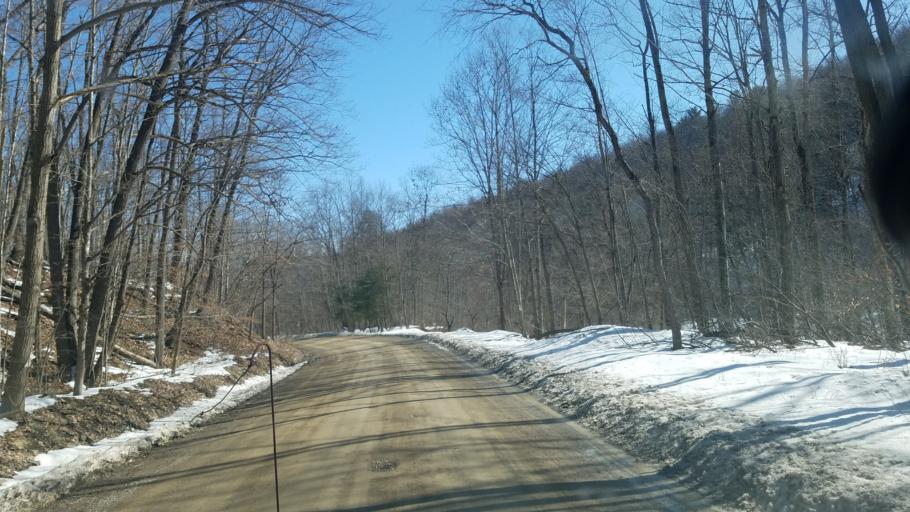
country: US
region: New York
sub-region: Allegany County
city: Alfred
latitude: 42.2479
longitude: -77.7072
